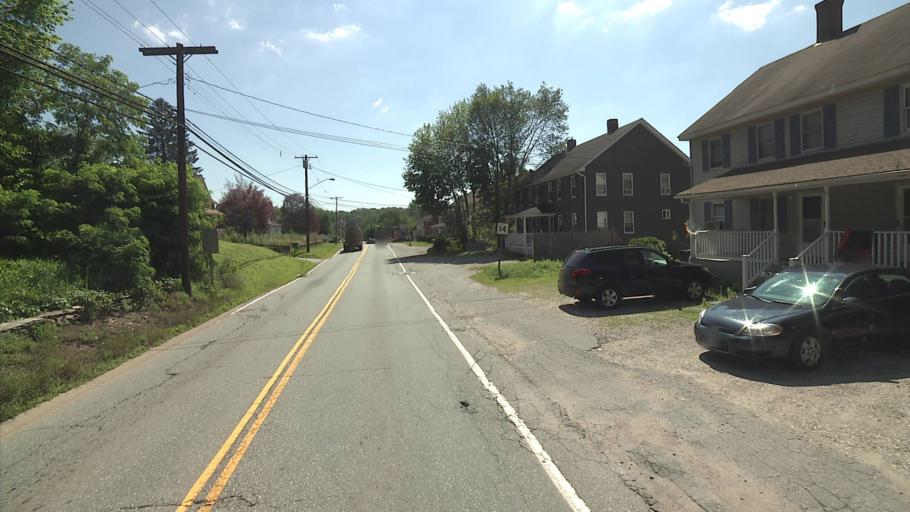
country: US
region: Connecticut
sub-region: Windham County
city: Moosup
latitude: 41.7194
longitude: -71.9017
